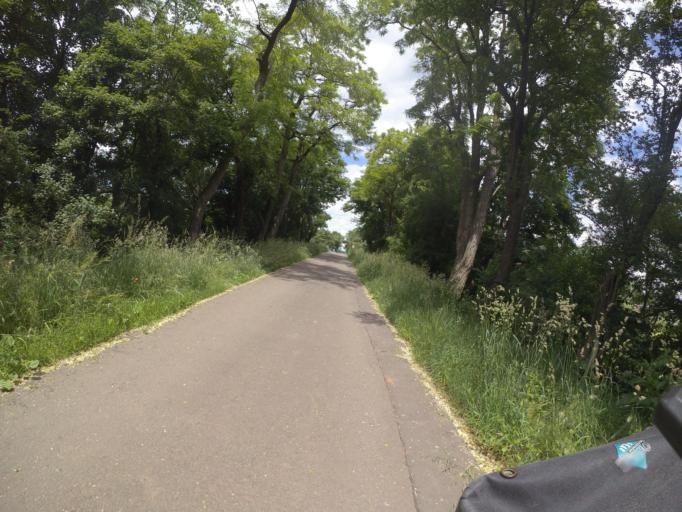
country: DE
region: Rheinland-Pfalz
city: Hauptstuhl
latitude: 49.3982
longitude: 7.4664
